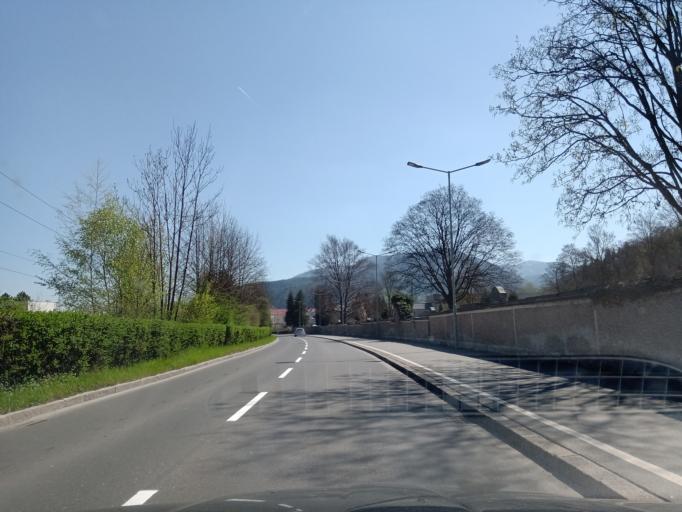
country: AT
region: Styria
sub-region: Politischer Bezirk Leoben
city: Leoben
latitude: 47.3742
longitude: 15.0772
